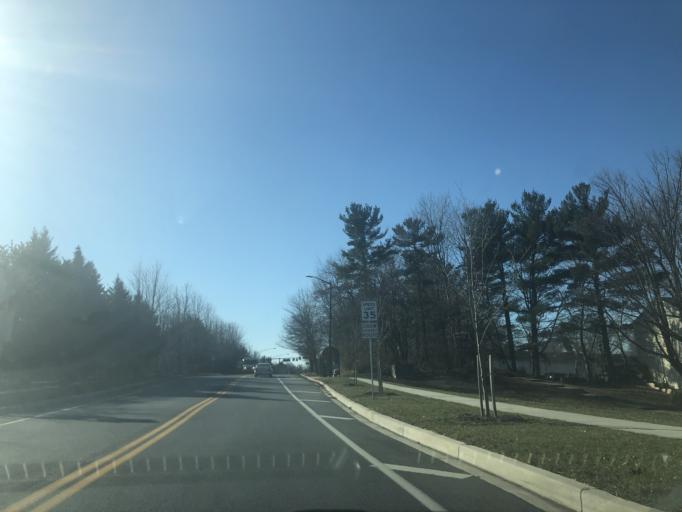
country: US
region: Maryland
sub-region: Howard County
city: Columbia
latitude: 39.2073
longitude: -76.8320
